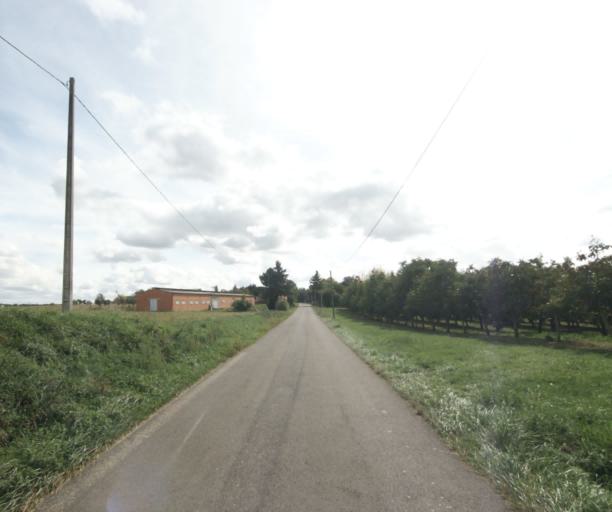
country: FR
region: Midi-Pyrenees
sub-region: Departement du Gers
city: Eauze
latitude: 43.8344
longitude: 0.1155
